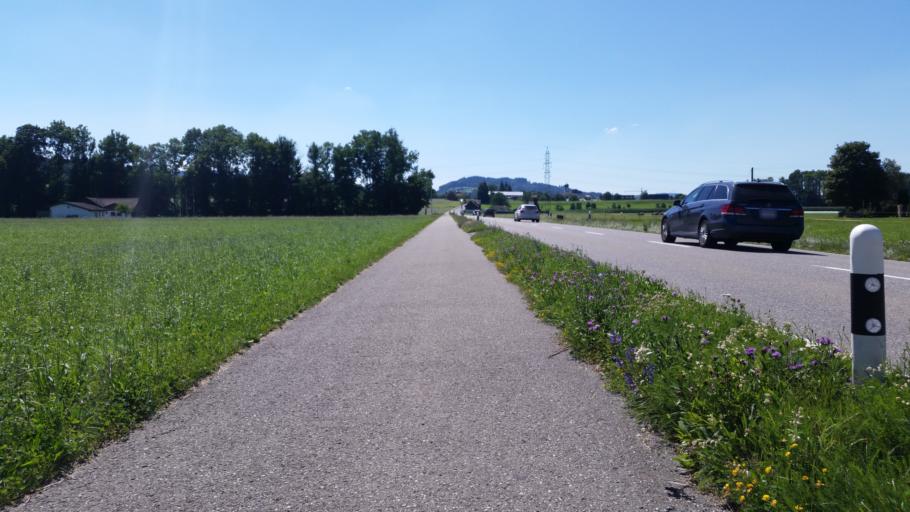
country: CH
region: Saint Gallen
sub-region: Wahlkreis Wil
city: Niederhelfenschwil
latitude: 47.4552
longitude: 9.1777
